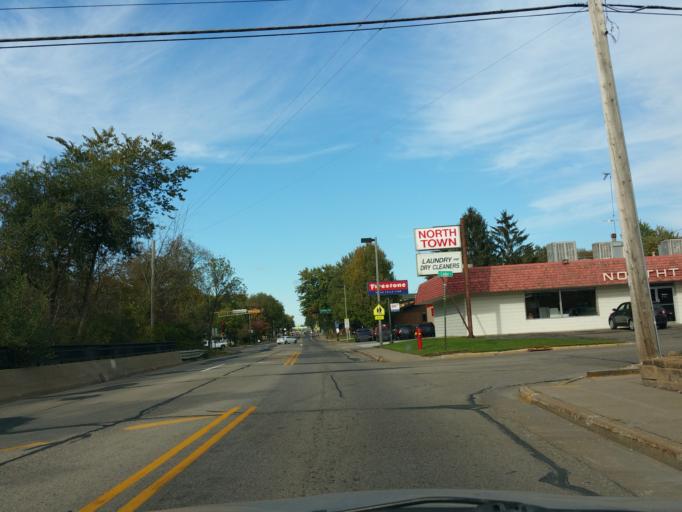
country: US
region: Wisconsin
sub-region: Pierce County
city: River Falls
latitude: 44.8615
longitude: -92.6244
